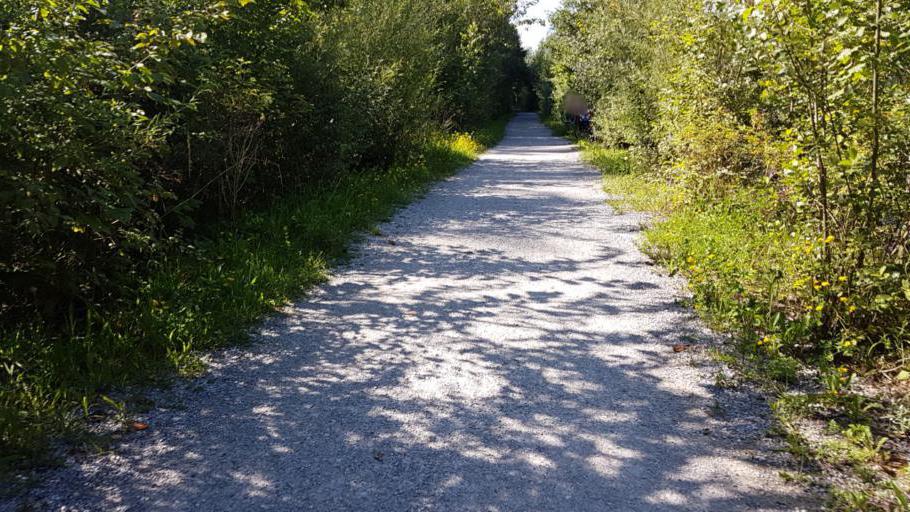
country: CH
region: Bern
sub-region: Bern-Mittelland District
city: Kehrsatz
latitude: 46.9236
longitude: 7.4724
